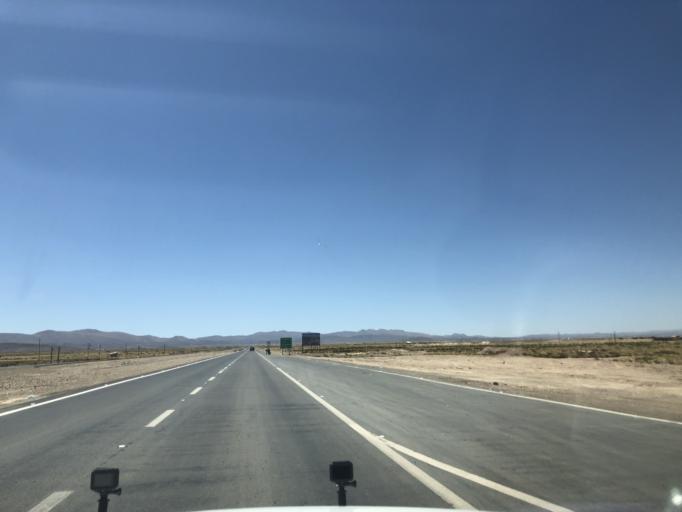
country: BO
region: La Paz
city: Colquiri
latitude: -17.6491
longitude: -67.2027
